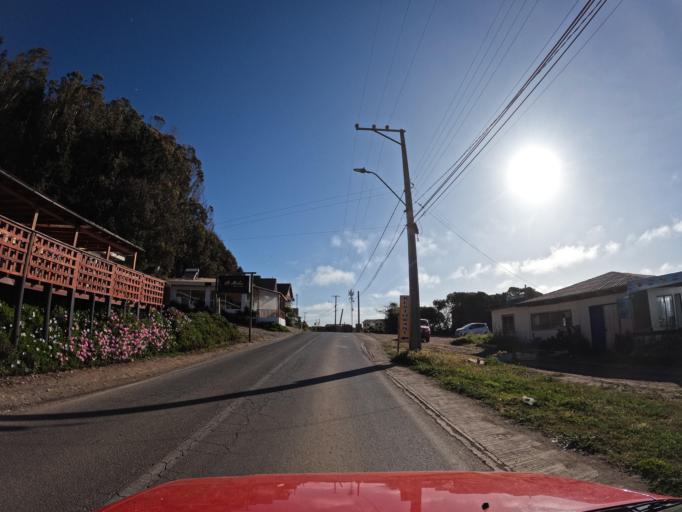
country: CL
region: Maule
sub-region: Provincia de Talca
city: Constitucion
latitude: -34.8898
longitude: -72.1732
